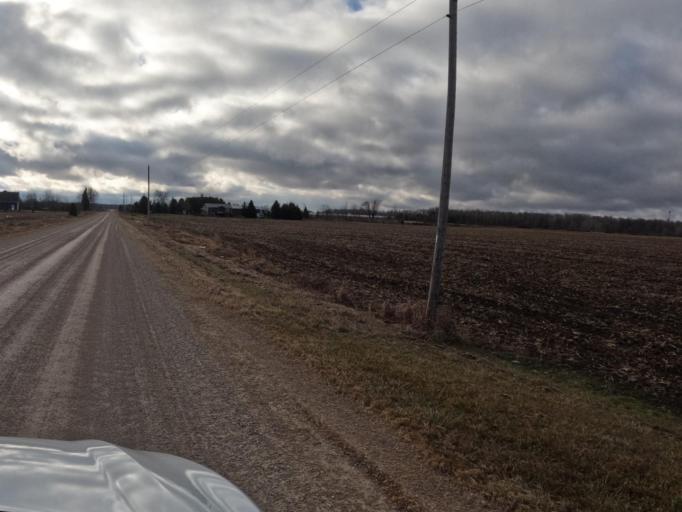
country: CA
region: Ontario
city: Shelburne
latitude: 43.8803
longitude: -80.3578
